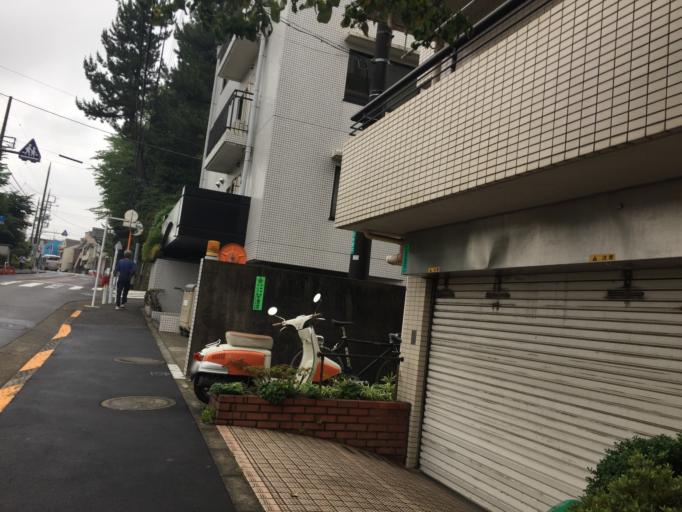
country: JP
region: Tokyo
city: Tokyo
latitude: 35.6370
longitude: 139.6765
